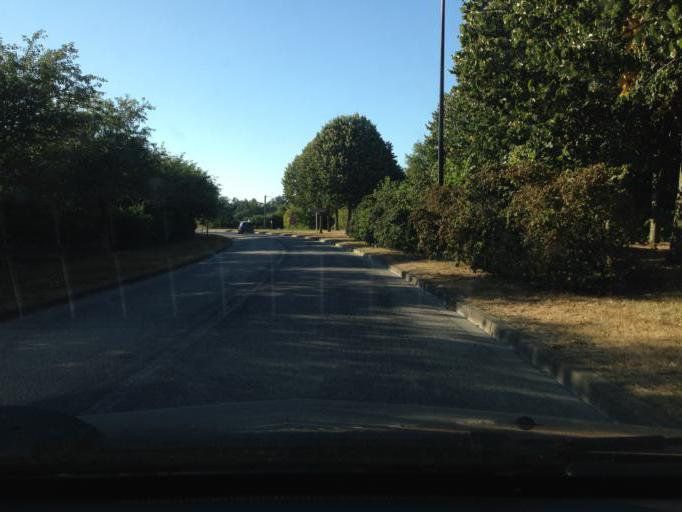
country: FR
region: Ile-de-France
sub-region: Departement des Yvelines
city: Chateaufort
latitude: 48.7289
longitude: 2.0814
